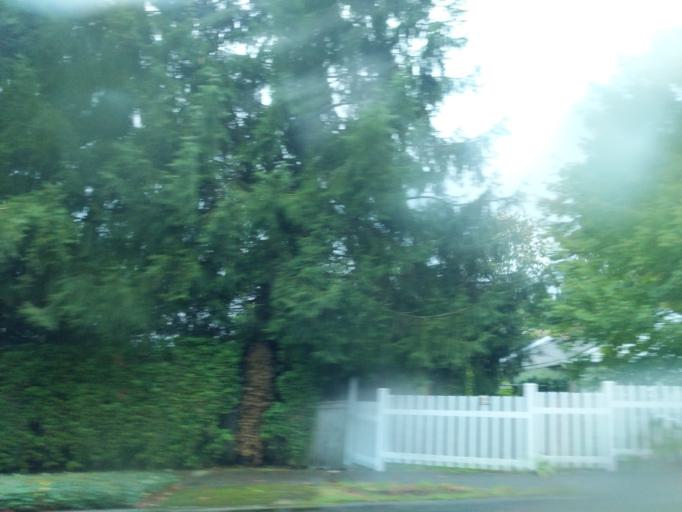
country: US
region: Washington
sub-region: King County
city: Bothell
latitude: 47.7719
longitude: -122.2070
